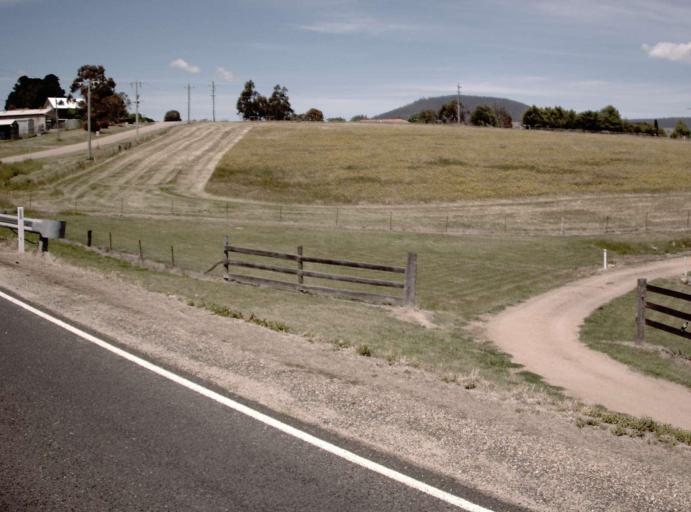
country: AU
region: Victoria
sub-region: Alpine
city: Mount Beauty
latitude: -37.1001
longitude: 147.6010
